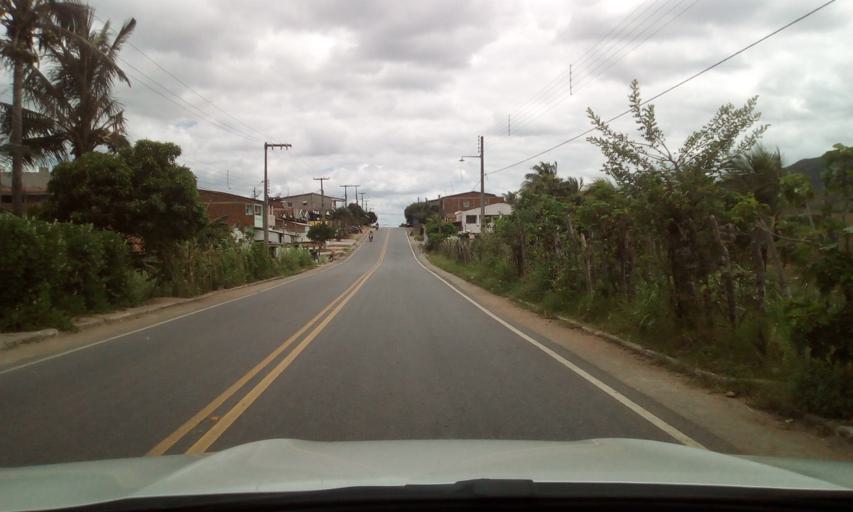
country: BR
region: Paraiba
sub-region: Serra Redonda
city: Alagoa Grande
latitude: -7.1798
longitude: -35.5897
